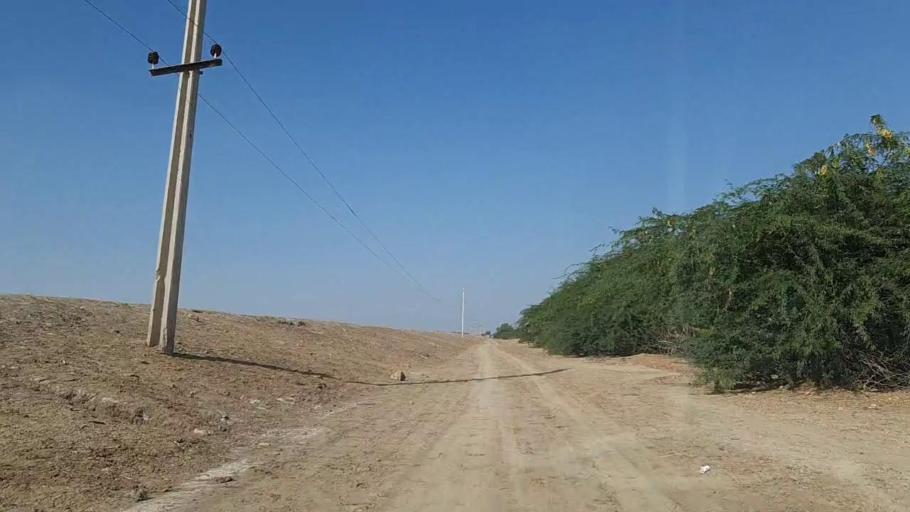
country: PK
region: Sindh
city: Chuhar Jamali
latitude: 24.5403
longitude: 68.0158
